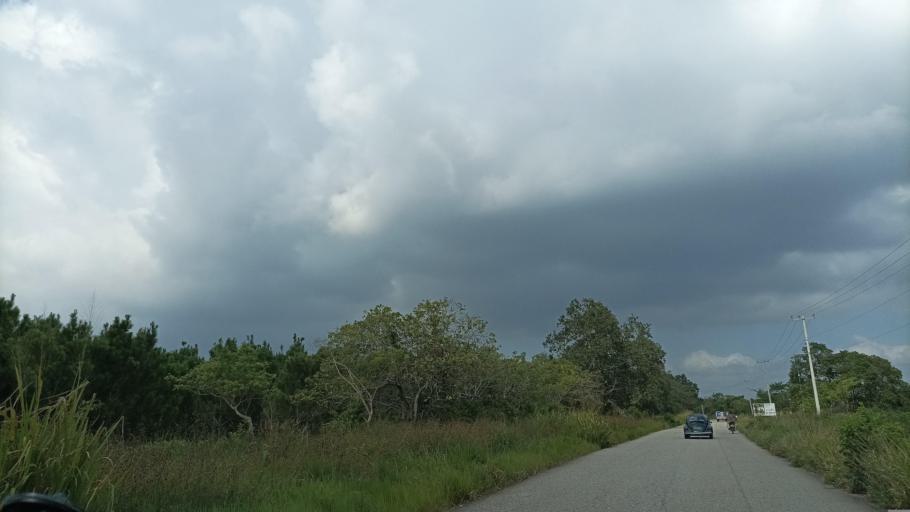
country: MX
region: Veracruz
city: Las Choapas
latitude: 17.8178
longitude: -94.1098
